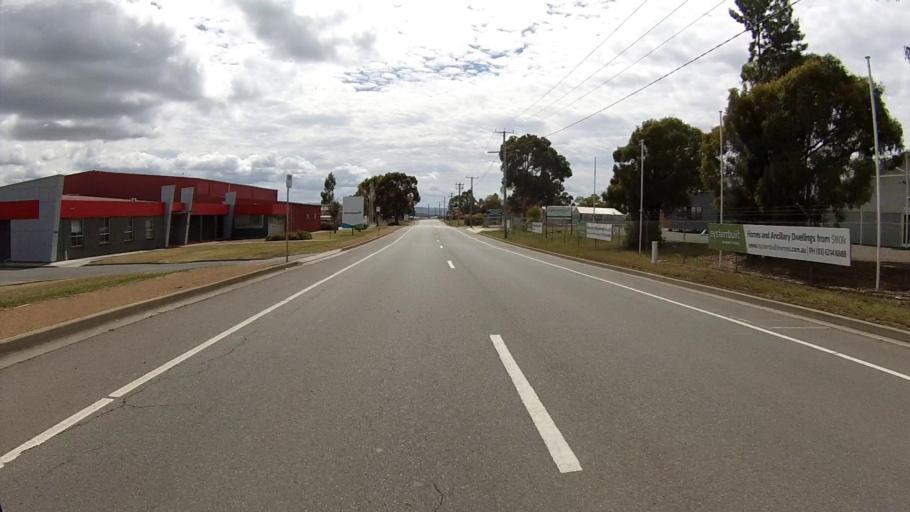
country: AU
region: Tasmania
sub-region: Clarence
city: Cambridge
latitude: -42.8350
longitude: 147.4495
